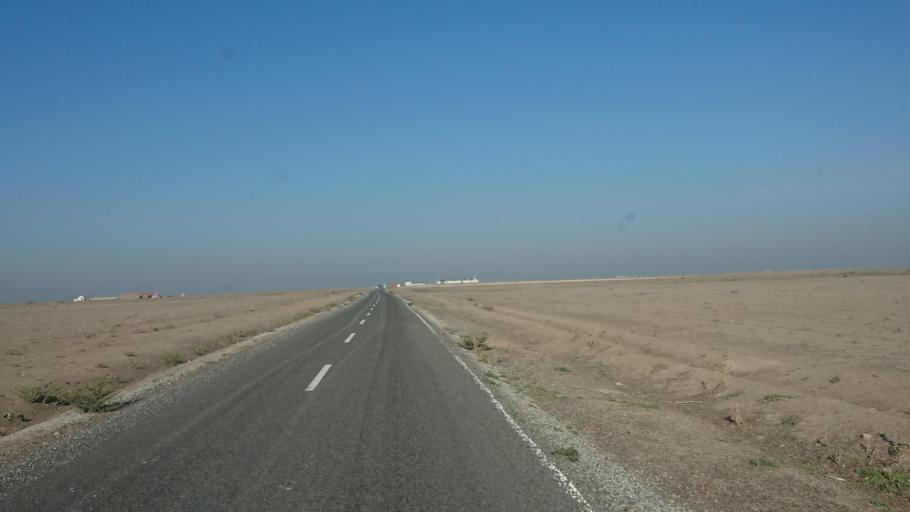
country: TR
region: Aksaray
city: Yesilova
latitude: 38.3879
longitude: 33.7575
